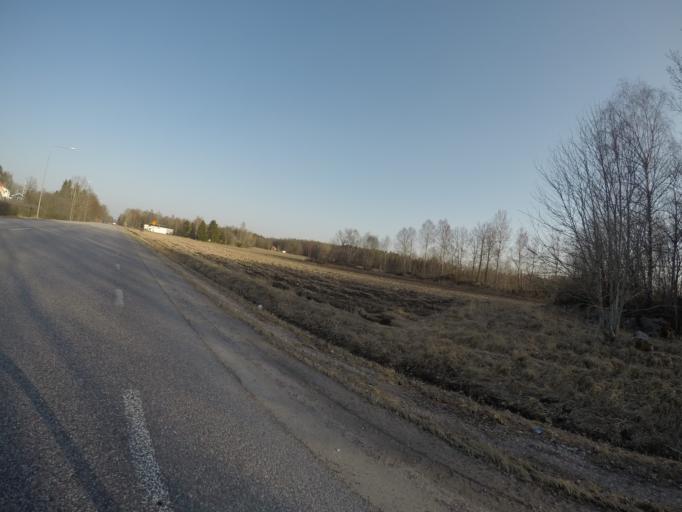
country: SE
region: Vaestmanland
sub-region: Kungsors Kommun
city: Kungsoer
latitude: 59.4224
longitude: 16.1410
